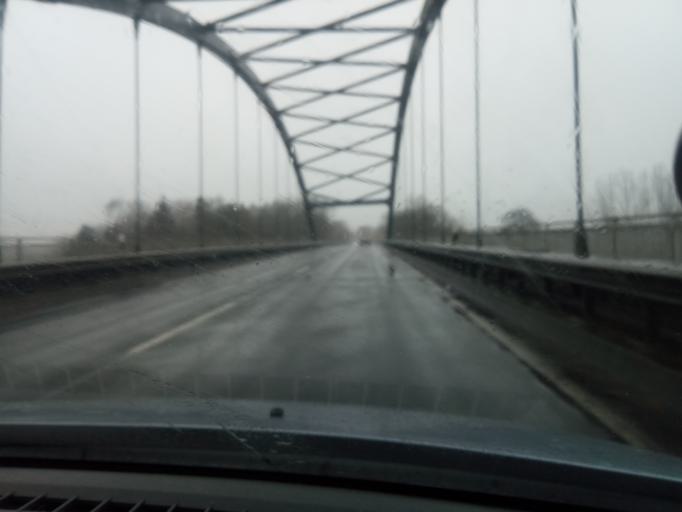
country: DE
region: Lower Saxony
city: Heede
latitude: 52.9803
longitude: 7.3019
